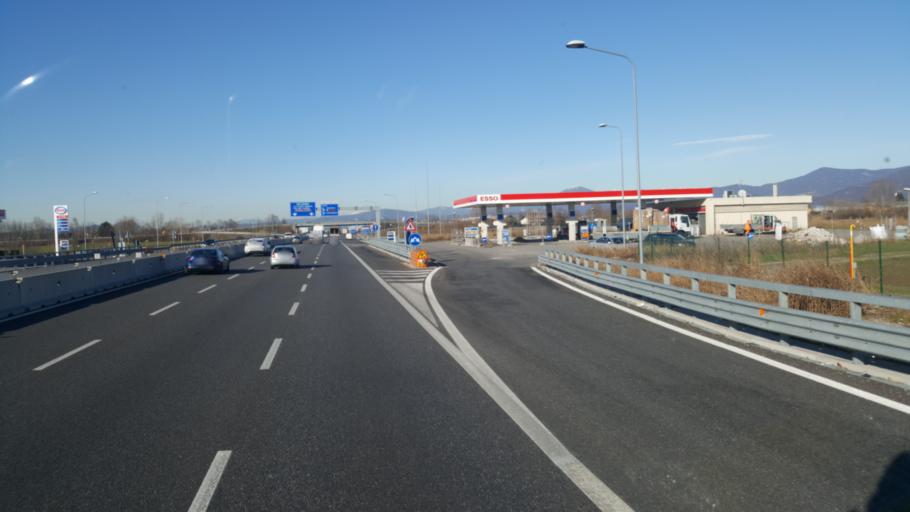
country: IT
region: Lombardy
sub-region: Provincia di Brescia
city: Roncadelle
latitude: 45.5371
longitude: 10.1534
